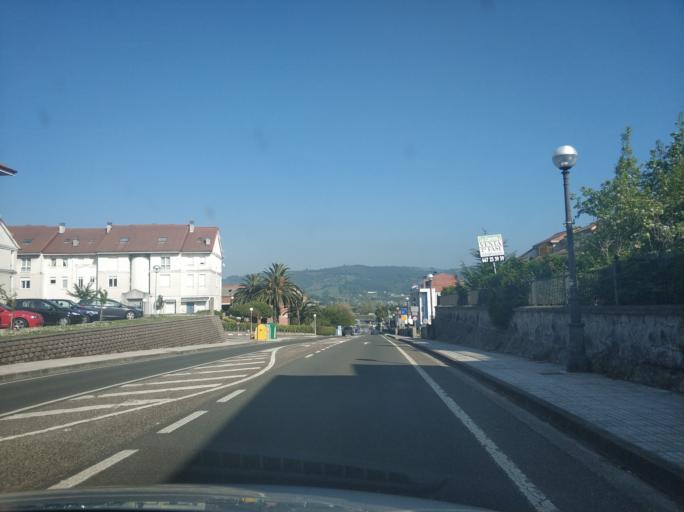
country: ES
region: Cantabria
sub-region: Provincia de Cantabria
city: Colindres
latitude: 43.3937
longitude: -3.4709
